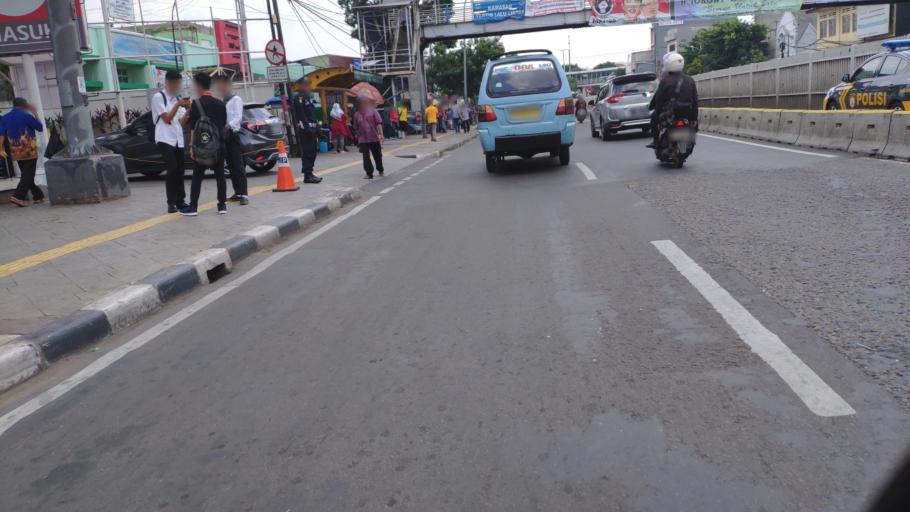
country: ID
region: Jakarta Raya
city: Jakarta
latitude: -6.2146
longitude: 106.8646
